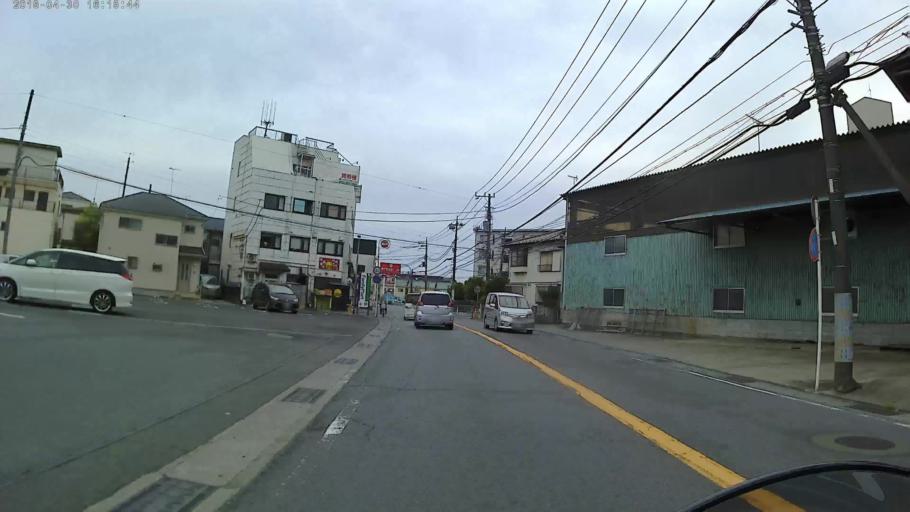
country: JP
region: Kanagawa
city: Minami-rinkan
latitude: 35.4860
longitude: 139.4312
